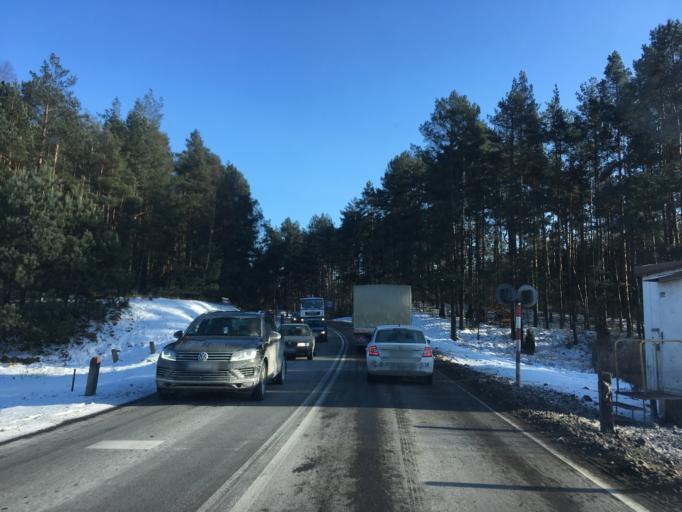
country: PL
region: Pomeranian Voivodeship
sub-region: Powiat koscierski
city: Koscierzyna
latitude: 54.1180
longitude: 17.8896
